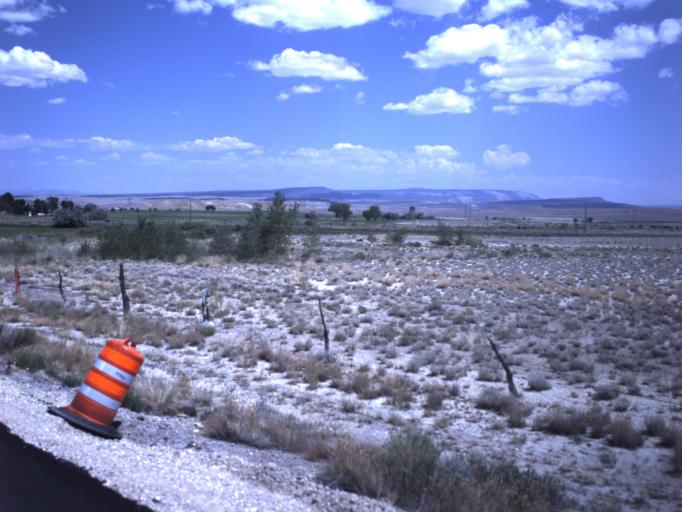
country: US
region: Utah
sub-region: Emery County
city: Castle Dale
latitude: 39.2444
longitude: -110.9919
